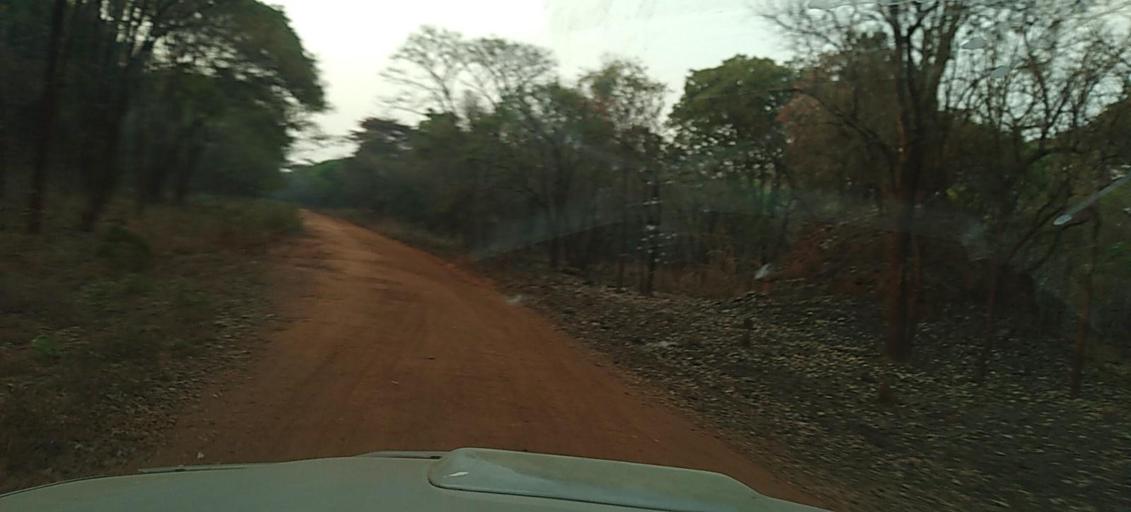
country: ZM
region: North-Western
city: Kasempa
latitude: -13.0904
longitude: 26.3993
